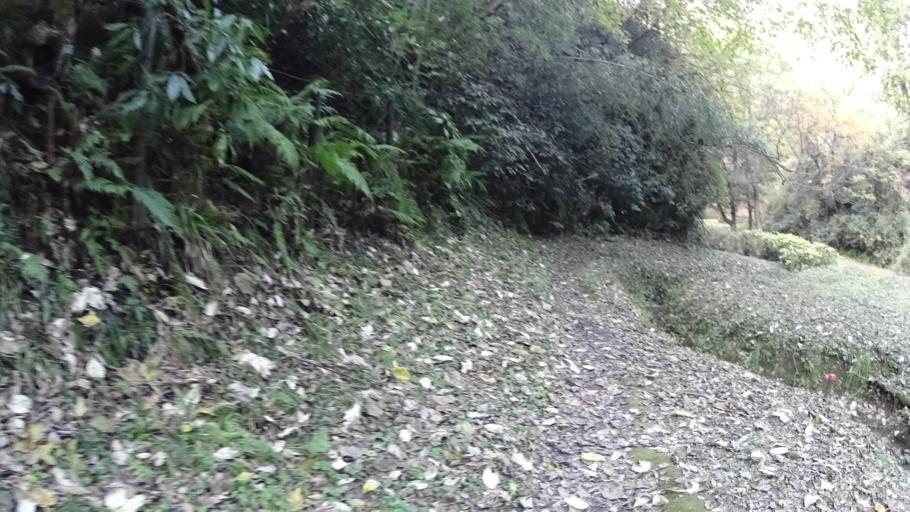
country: JP
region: Kanagawa
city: Kamakura
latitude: 35.3589
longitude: 139.5895
